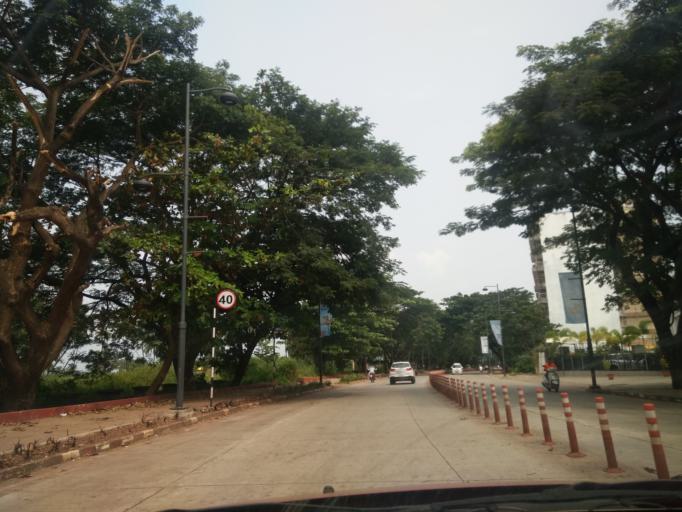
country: IN
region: Goa
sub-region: North Goa
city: Taleigao
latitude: 15.4608
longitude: 73.8036
